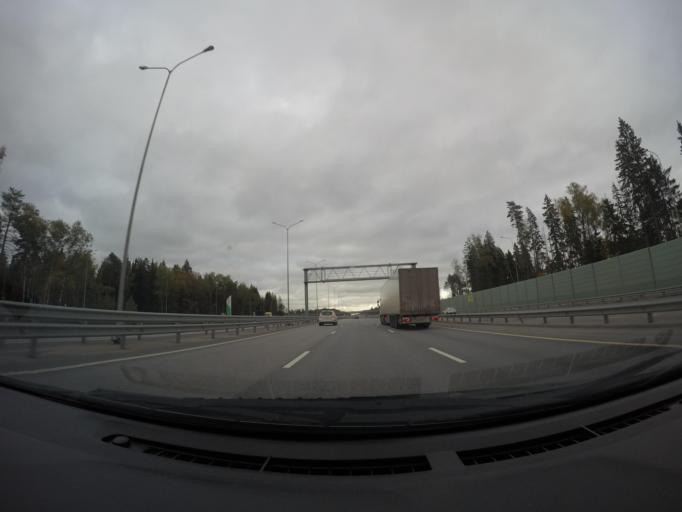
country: RU
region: Moskovskaya
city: Bol'shiye Vyazemy
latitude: 55.5886
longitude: 36.8742
